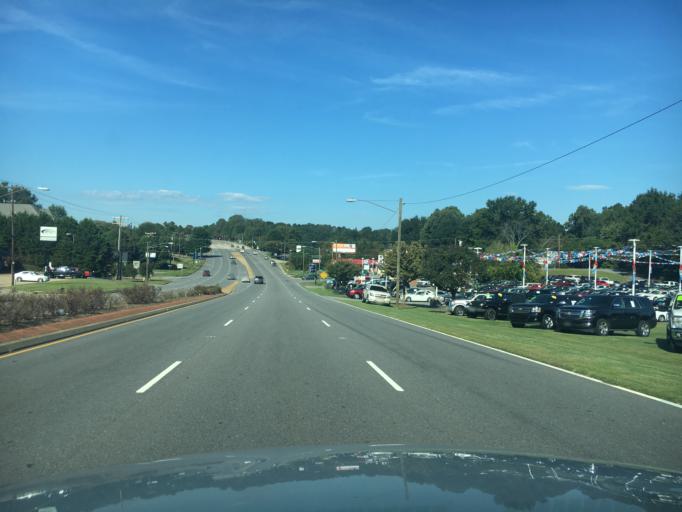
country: US
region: North Carolina
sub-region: Catawba County
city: Hickory
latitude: 35.7213
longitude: -81.3507
